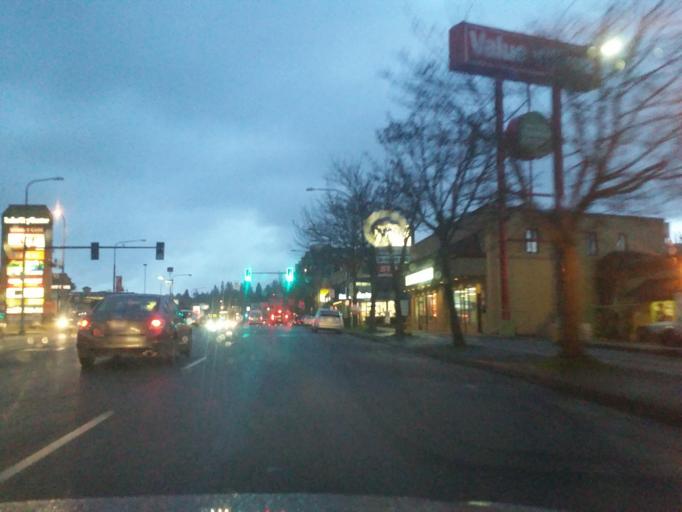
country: US
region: Washington
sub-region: King County
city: Lake Forest Park
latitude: 47.7205
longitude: -122.2944
